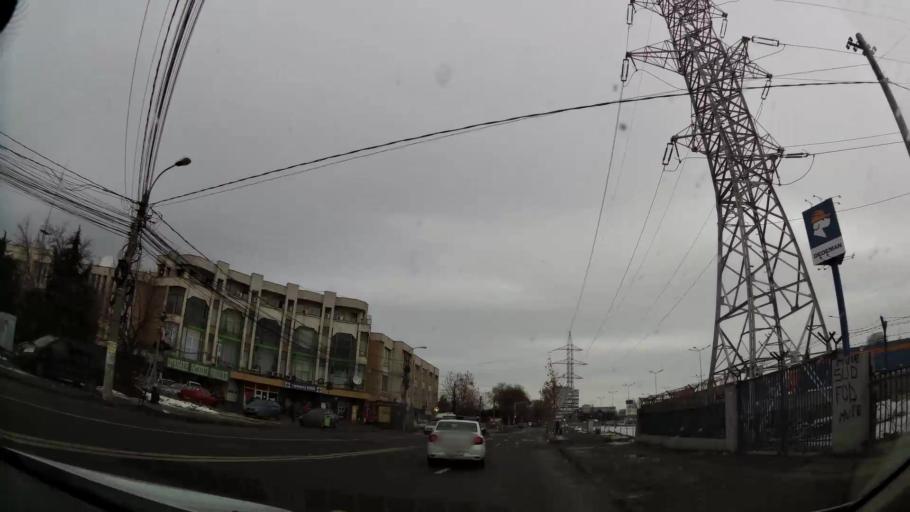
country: RO
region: Ilfov
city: Dobroesti
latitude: 44.4340
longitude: 26.1869
